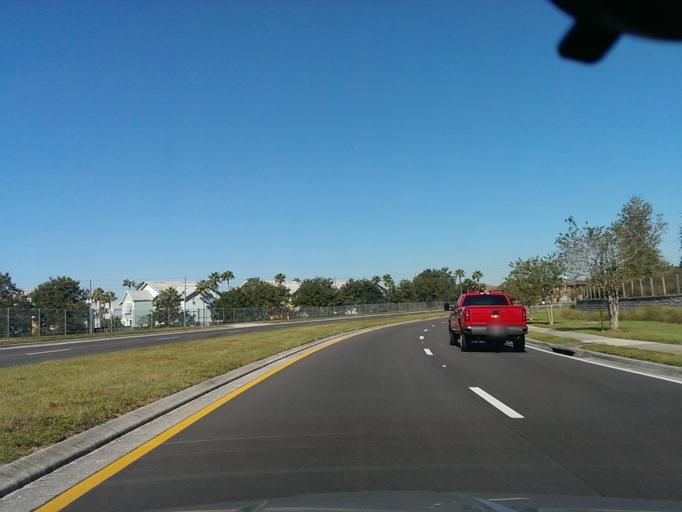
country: US
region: Florida
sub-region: Orange County
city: Doctor Phillips
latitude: 28.3991
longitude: -81.5314
